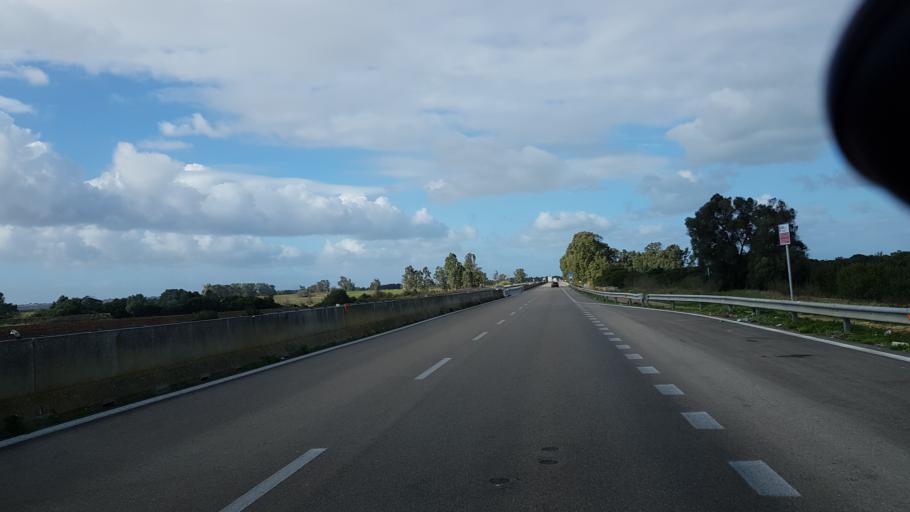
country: IT
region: Apulia
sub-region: Provincia di Brindisi
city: San Vito dei Normanni
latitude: 40.7044
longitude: 17.7988
